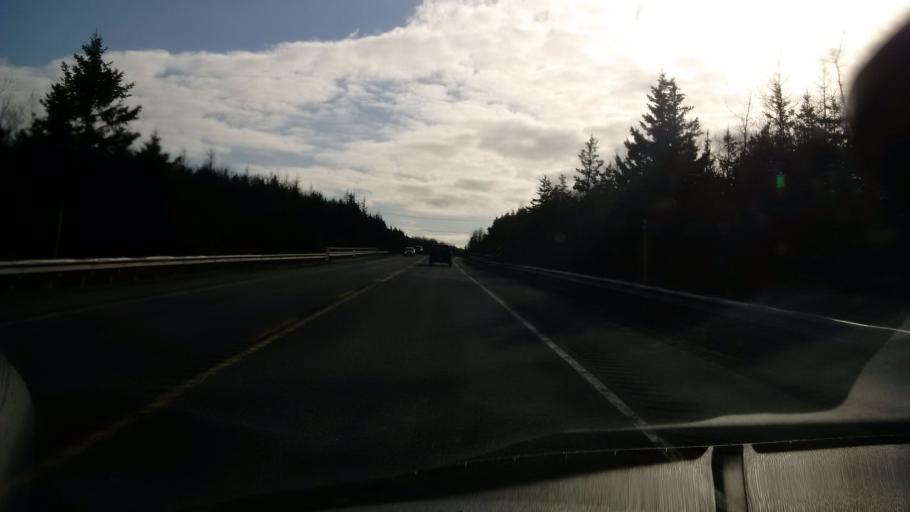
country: CA
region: Nova Scotia
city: New Glasgow
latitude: 45.5756
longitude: -62.3653
